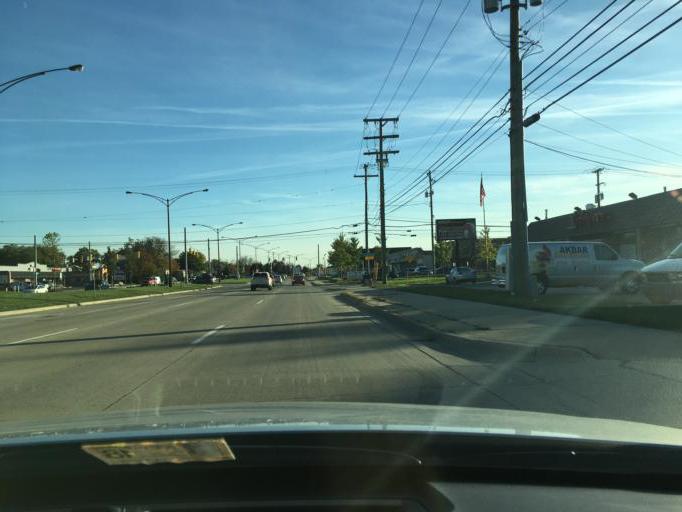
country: US
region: Michigan
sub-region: Oakland County
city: Clawson
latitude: 42.5688
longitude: -83.1281
